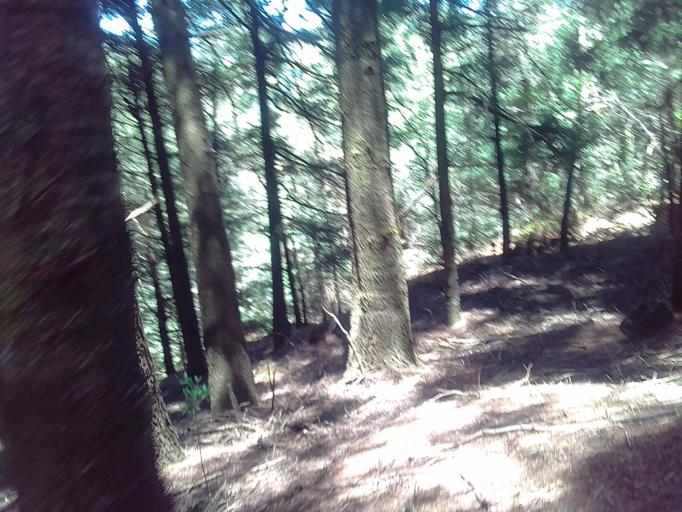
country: MX
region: Mexico City
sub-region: Cuajimalpa de Morelos
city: San Lorenzo Acopilco
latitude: 19.2883
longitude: -99.3350
